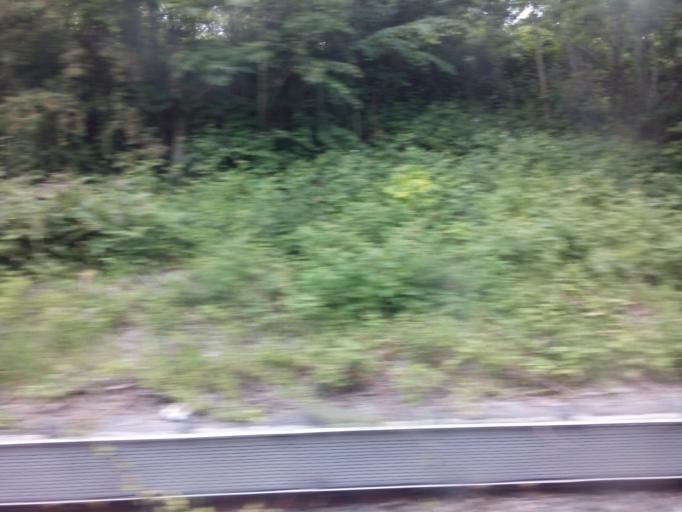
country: GB
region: England
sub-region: South Tyneside
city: South Shields
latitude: 54.9741
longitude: -1.4424
